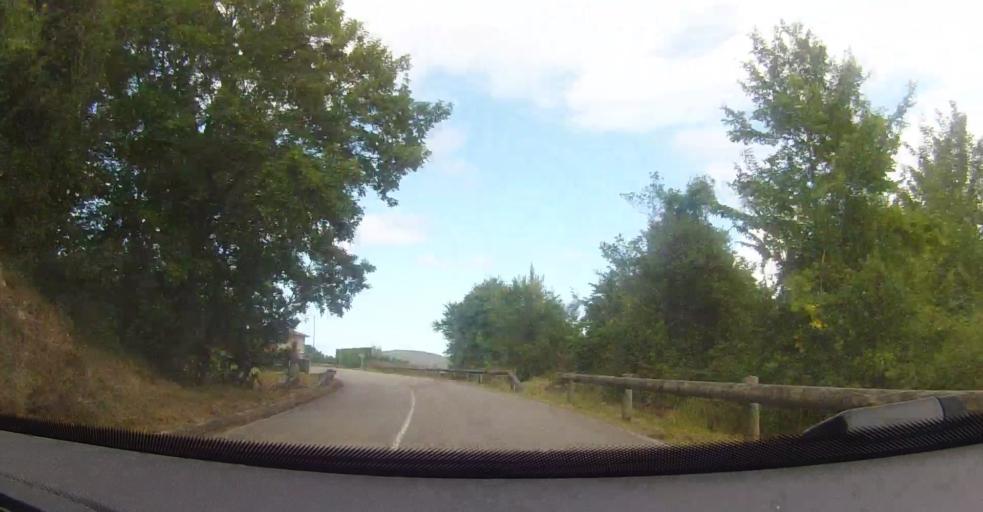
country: ES
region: Asturias
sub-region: Province of Asturias
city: Villaviciosa
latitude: 43.5185
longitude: -5.4018
